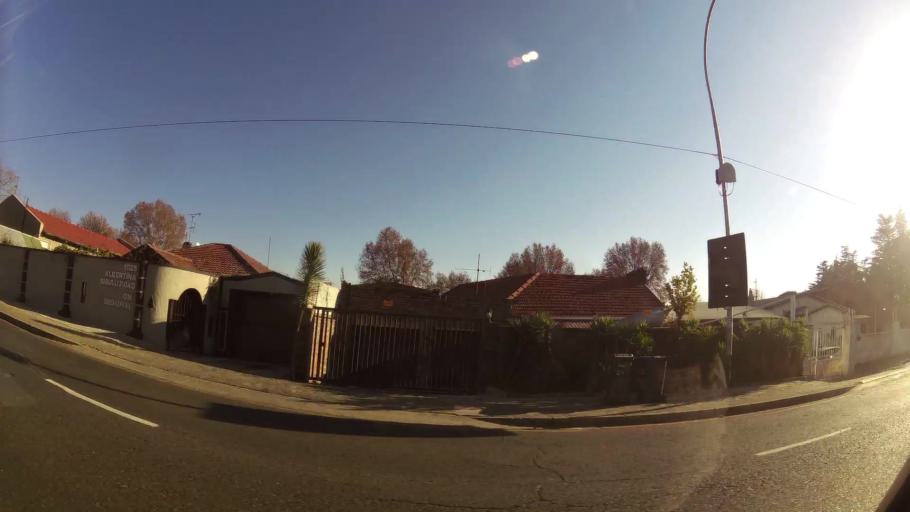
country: ZA
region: Gauteng
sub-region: City of Johannesburg Metropolitan Municipality
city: Johannesburg
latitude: -26.1864
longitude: 28.0985
